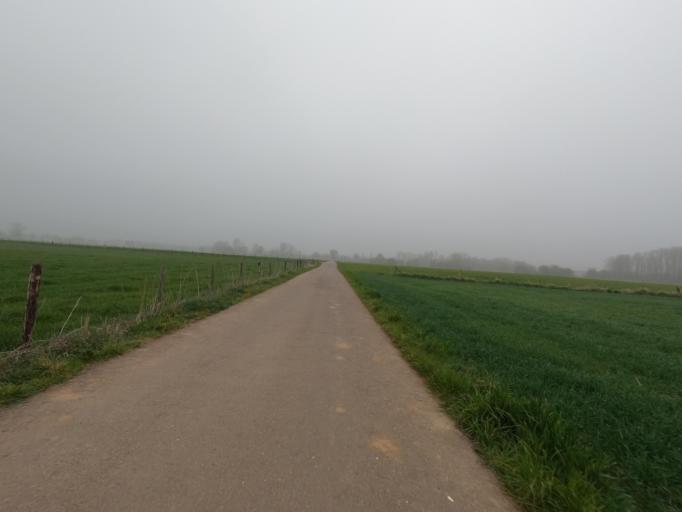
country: DE
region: North Rhine-Westphalia
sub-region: Regierungsbezirk Koln
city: Wassenberg
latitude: 51.0765
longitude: 6.1506
